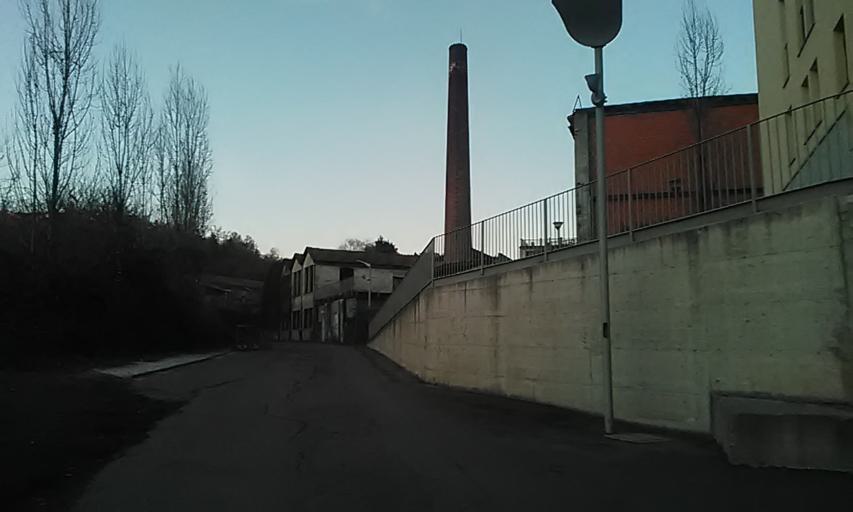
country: IT
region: Piedmont
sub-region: Provincia di Biella
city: Biella
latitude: 45.5691
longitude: 8.0637
